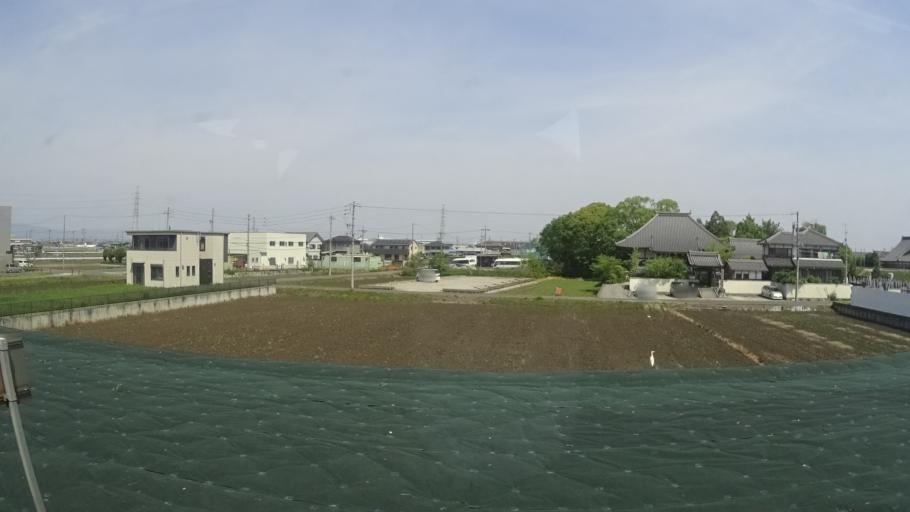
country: JP
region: Aichi
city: Kanie
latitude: 35.1402
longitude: 136.7853
